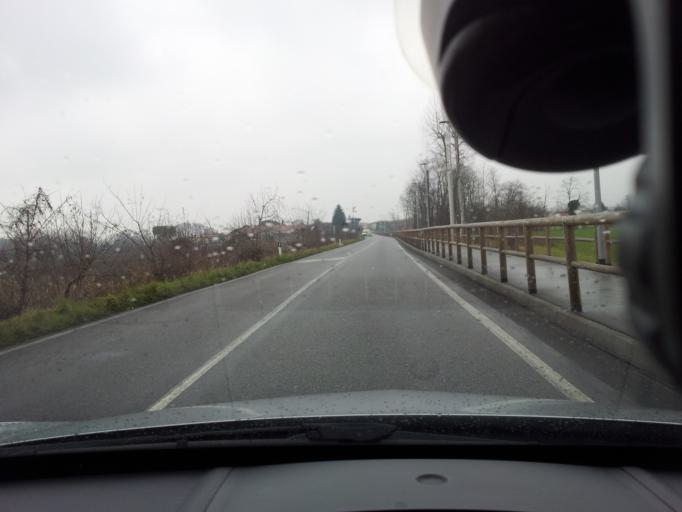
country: IT
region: Lombardy
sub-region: Provincia di Bergamo
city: Cavernago
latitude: 45.6207
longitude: 9.7796
